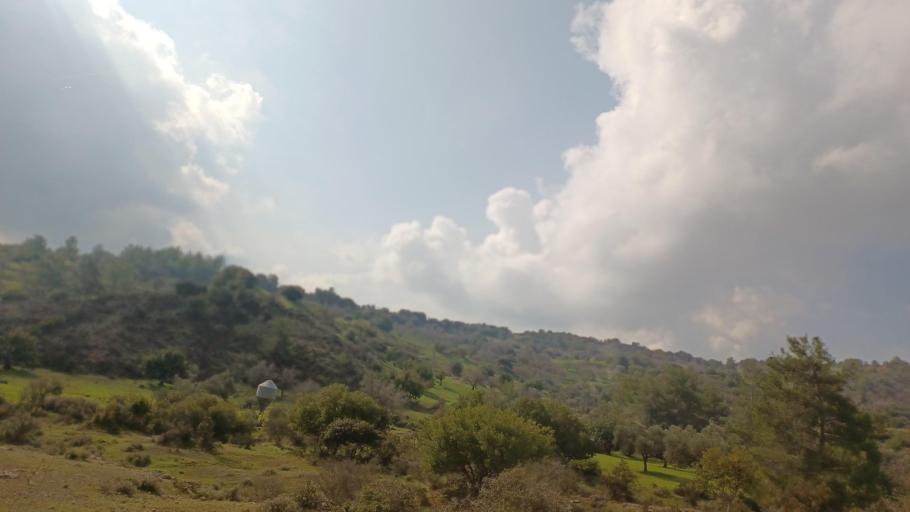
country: CY
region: Pafos
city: Polis
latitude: 34.9956
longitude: 32.5342
